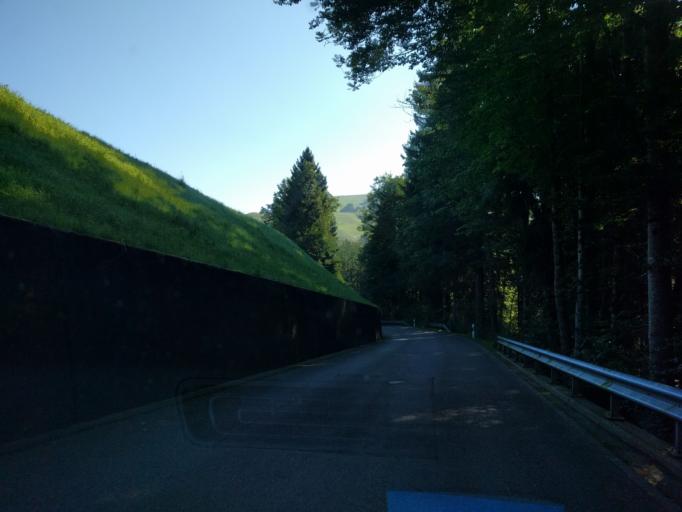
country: CH
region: Saint Gallen
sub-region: Wahlkreis Toggenburg
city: Sankt Peterzell
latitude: 47.2962
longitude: 9.1843
